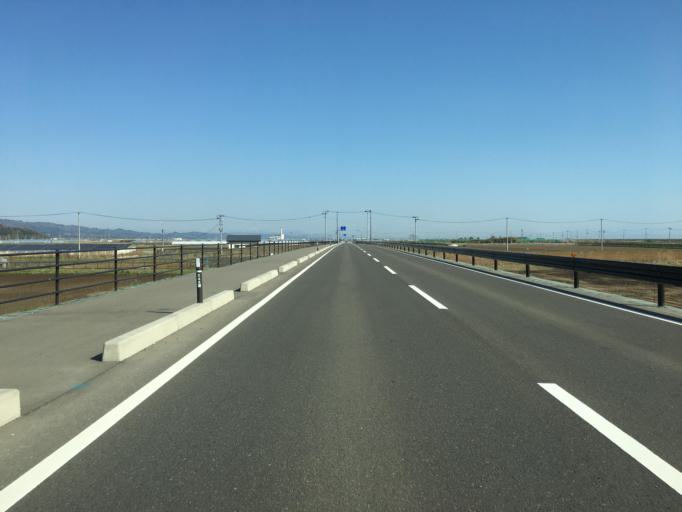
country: JP
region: Miyagi
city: Watari
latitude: 37.9376
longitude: 140.9100
